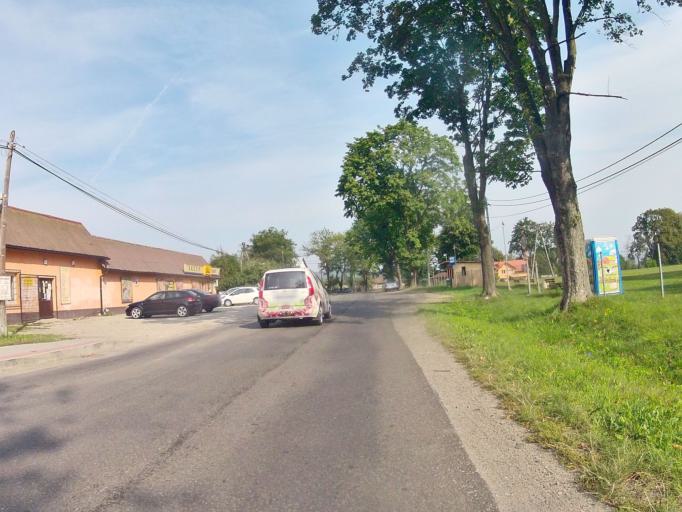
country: PL
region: Subcarpathian Voivodeship
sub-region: Powiat jasielski
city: Trzcinica
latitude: 49.7762
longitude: 21.4067
